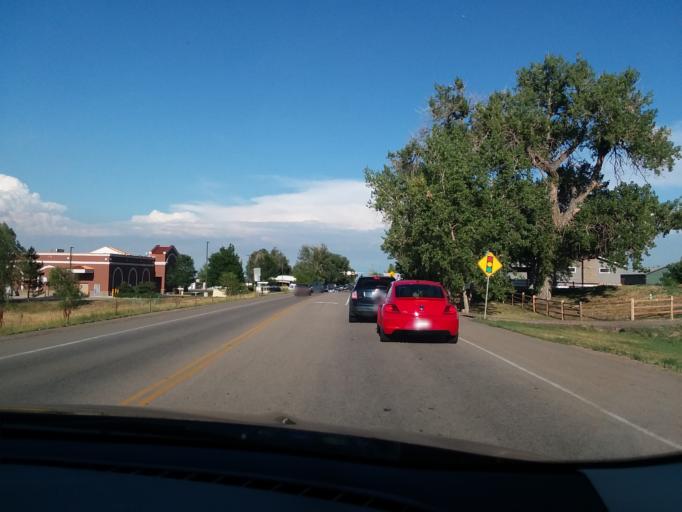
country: US
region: Colorado
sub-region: Larimer County
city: Fort Collins
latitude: 40.4948
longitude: -105.0799
